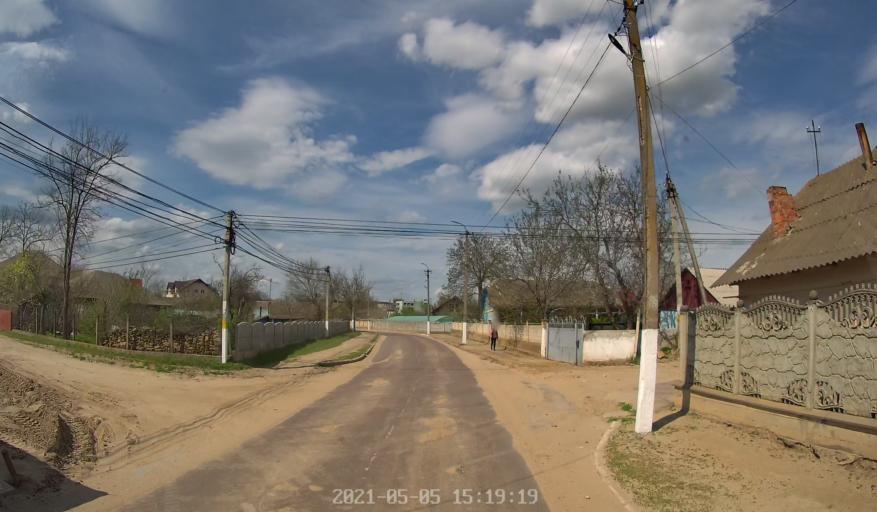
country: MD
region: Criuleni
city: Criuleni
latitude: 47.1261
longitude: 29.1940
